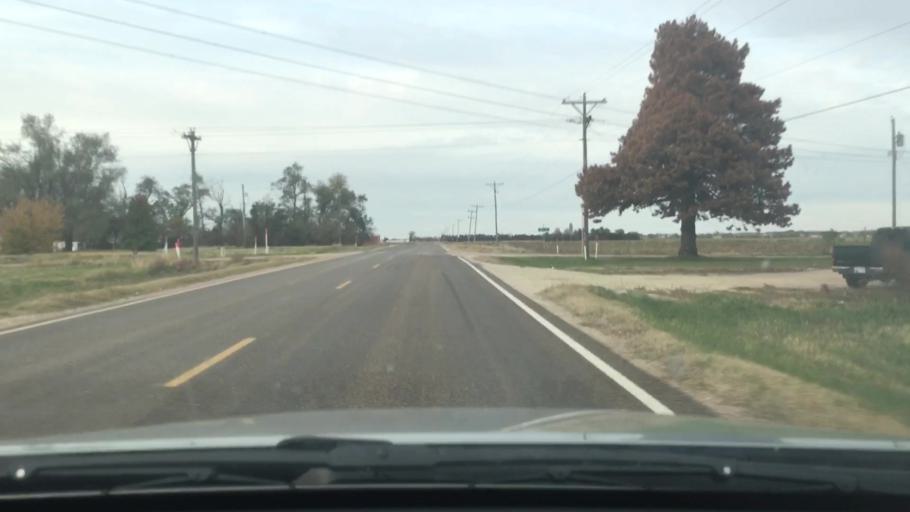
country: US
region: Kansas
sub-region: Sedgwick County
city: Colwich
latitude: 37.7937
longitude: -97.5183
